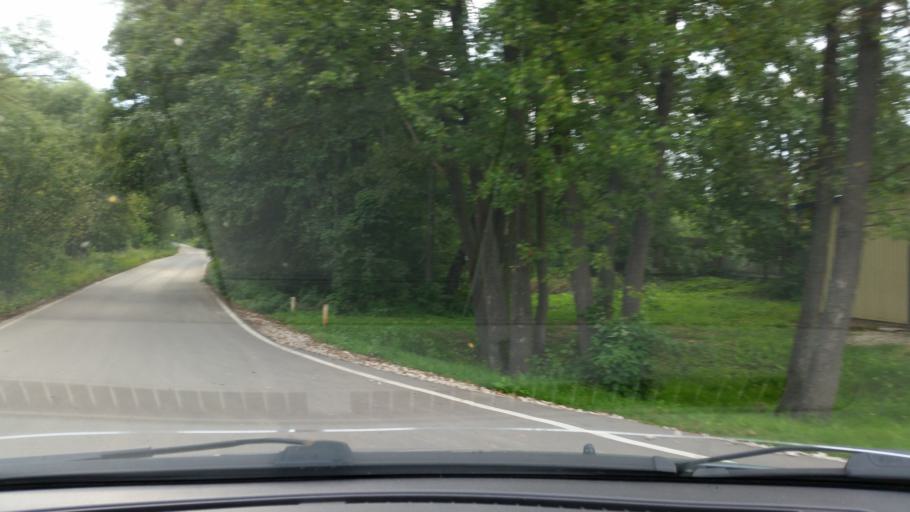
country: RU
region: Moskovskaya
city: Bol'shoye Gryzlovo
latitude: 54.8579
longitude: 37.7476
